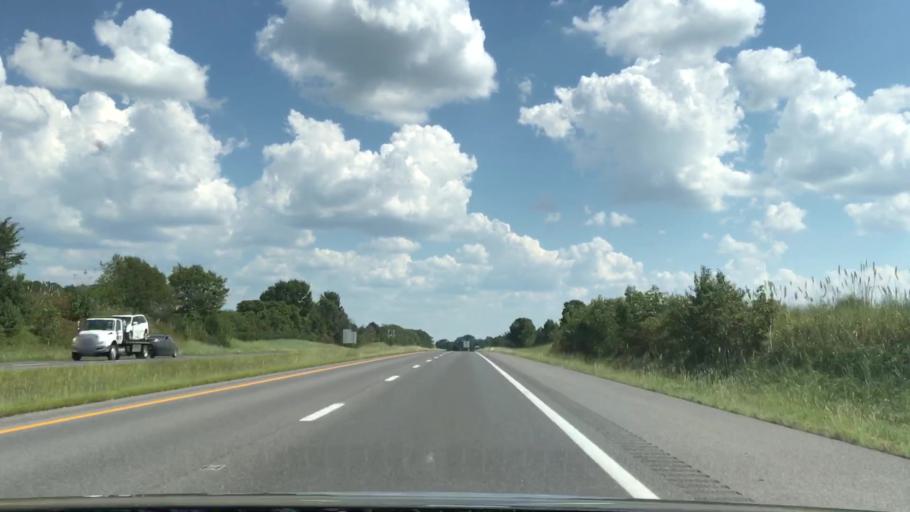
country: US
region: Kentucky
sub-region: Lyon County
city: Eddyville
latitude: 37.1080
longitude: -87.9987
